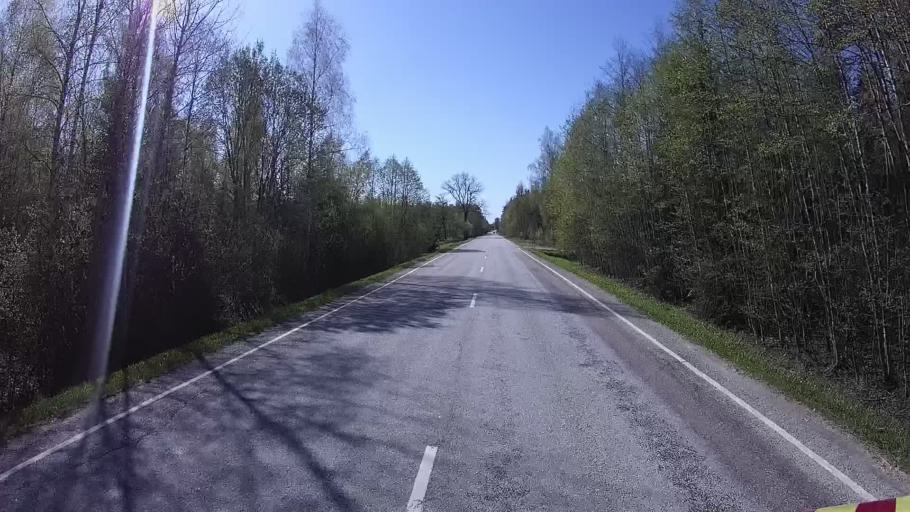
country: EE
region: Raplamaa
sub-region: Jaervakandi vald
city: Jarvakandi
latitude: 58.8019
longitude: 24.8130
